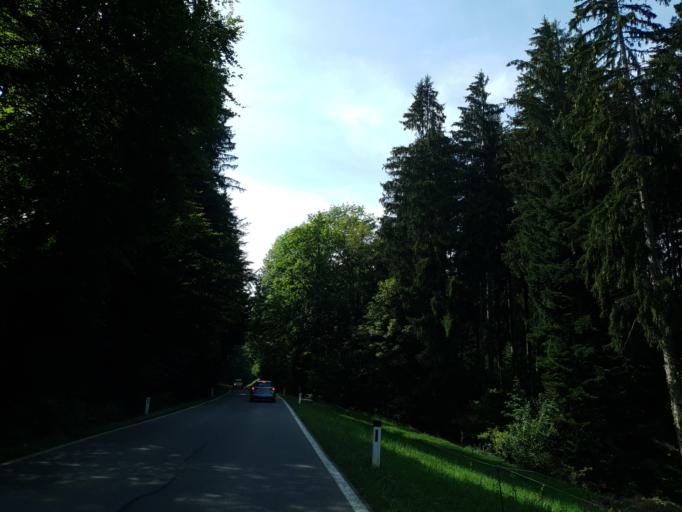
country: AT
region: Vorarlberg
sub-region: Politischer Bezirk Bregenz
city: Kennelbach
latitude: 47.4901
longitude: 9.7640
